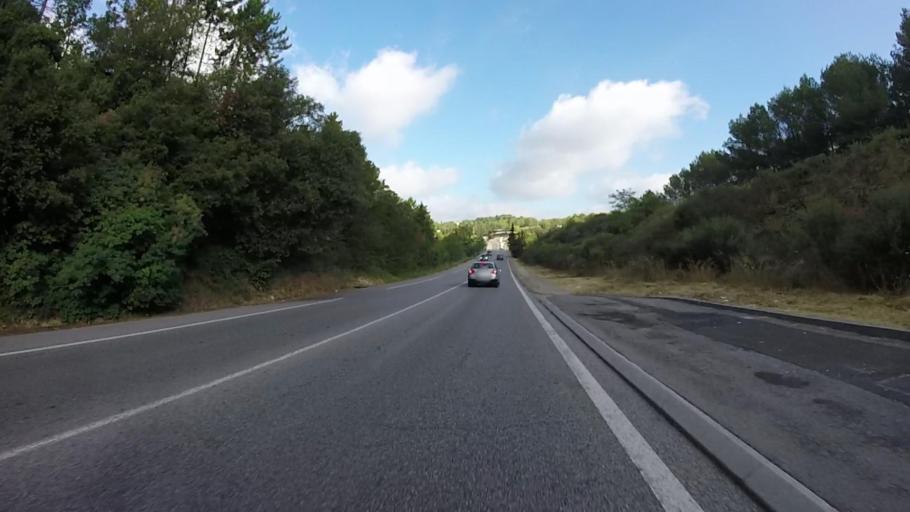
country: FR
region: Provence-Alpes-Cote d'Azur
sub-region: Departement des Alpes-Maritimes
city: Biot
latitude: 43.6192
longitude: 7.0671
